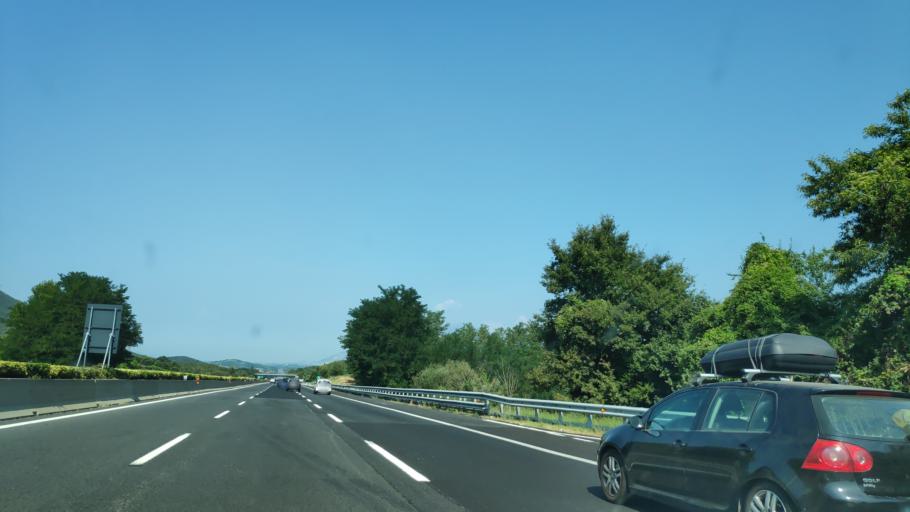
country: IT
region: Campania
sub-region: Provincia di Caserta
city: Mignano Monte Lungo
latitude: 41.4107
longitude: 13.9546
